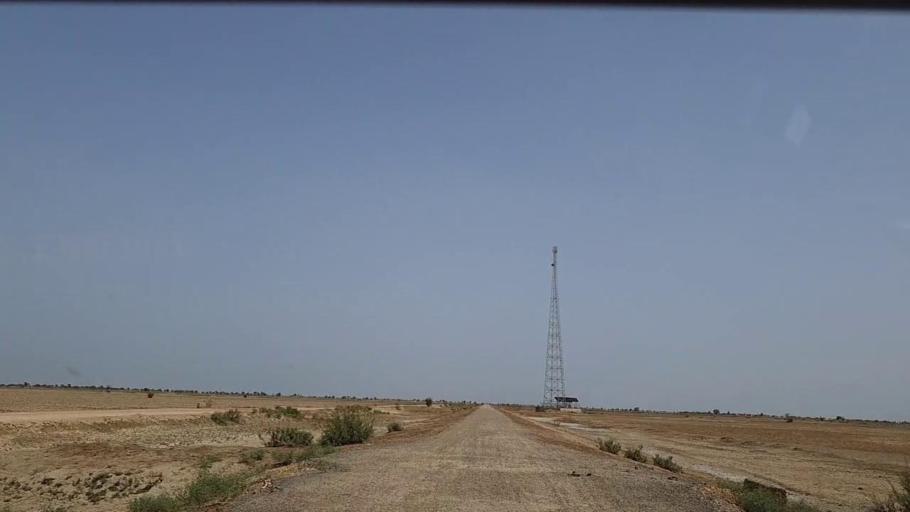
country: PK
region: Sindh
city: Phulji
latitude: 26.7911
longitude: 67.6424
